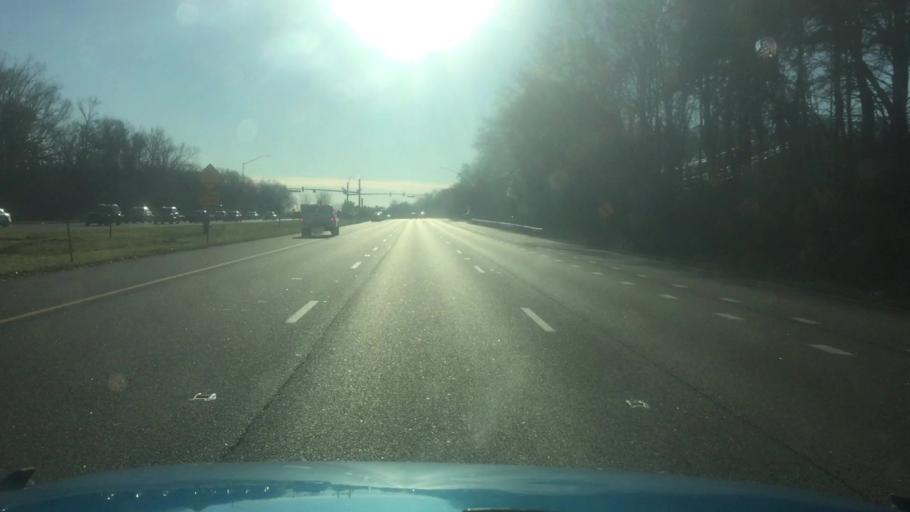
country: US
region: Maryland
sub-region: Prince George's County
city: Berwyn Heights
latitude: 38.9917
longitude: -76.9046
